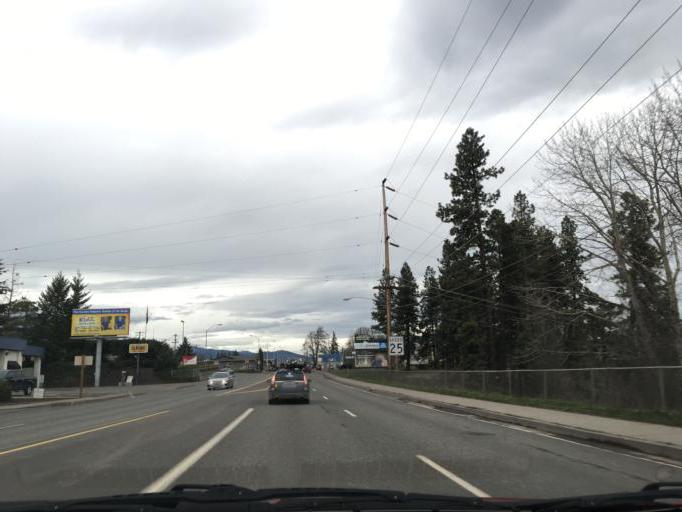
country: US
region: Oregon
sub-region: Hood River County
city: Hood River
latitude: 45.6977
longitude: -121.5236
